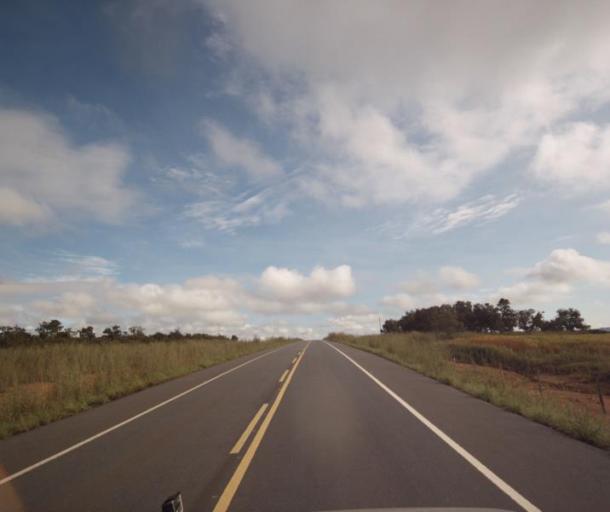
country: BR
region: Goias
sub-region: Barro Alto
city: Barro Alto
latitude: -15.2314
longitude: -48.6937
